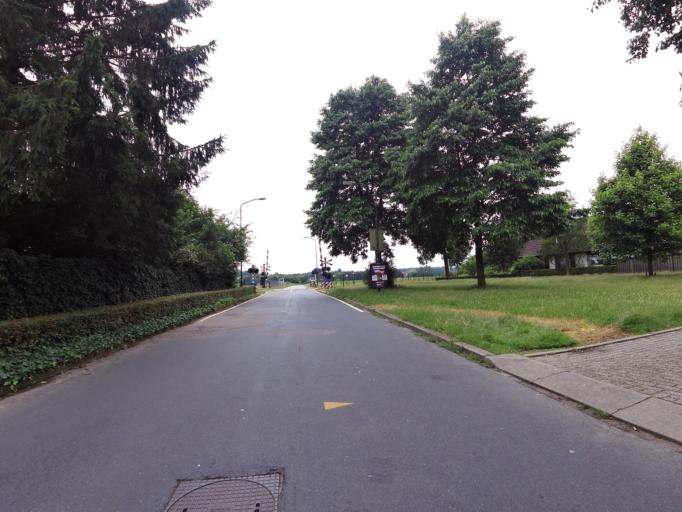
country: NL
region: Gelderland
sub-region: Gemeente Doetinchem
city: Doetinchem
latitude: 51.9557
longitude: 6.2074
